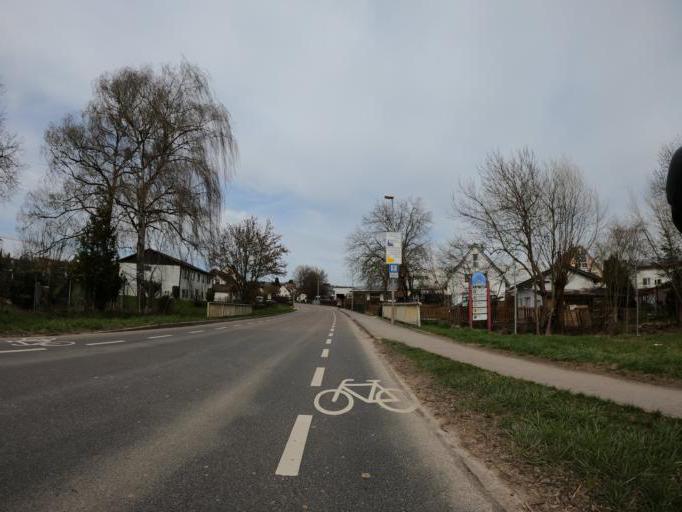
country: DE
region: Baden-Wuerttemberg
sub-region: Regierungsbezirk Stuttgart
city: Wolfschlugen
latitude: 48.6451
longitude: 9.2522
